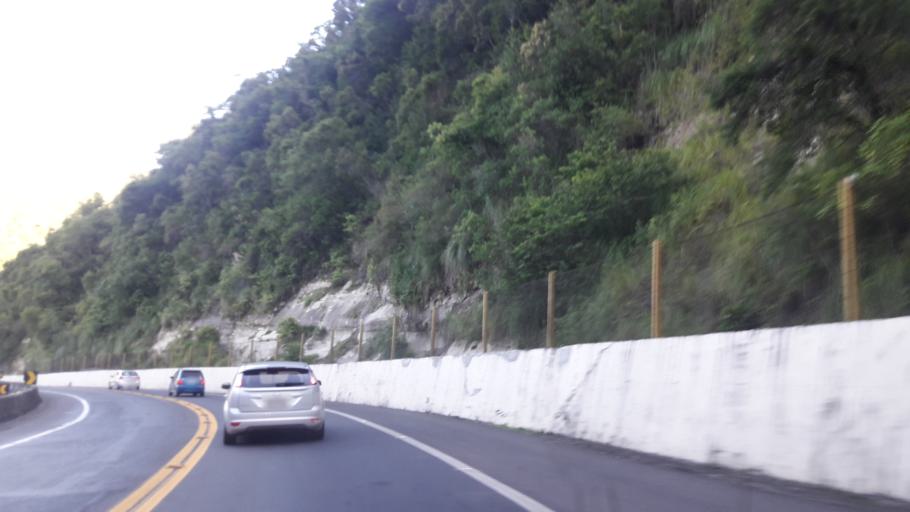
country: BR
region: Parana
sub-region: Prudentopolis
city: Prudentopolis
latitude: -25.3238
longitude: -51.1961
